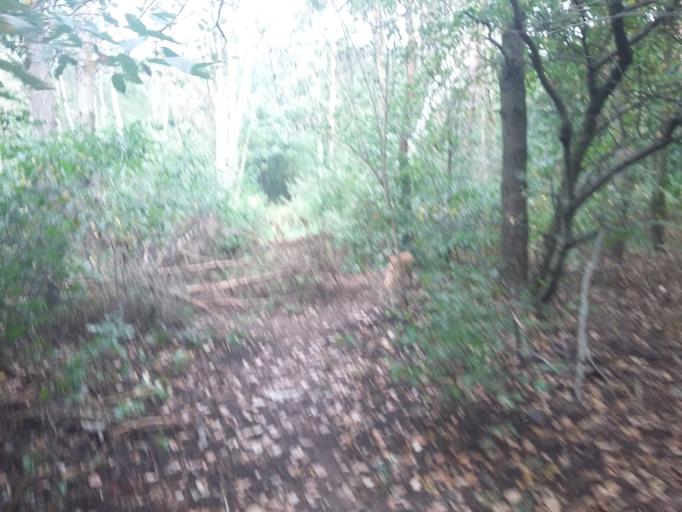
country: PL
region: Lodz Voivodeship
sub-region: Powiat pabianicki
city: Ksawerow
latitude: 51.7263
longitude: 19.3903
